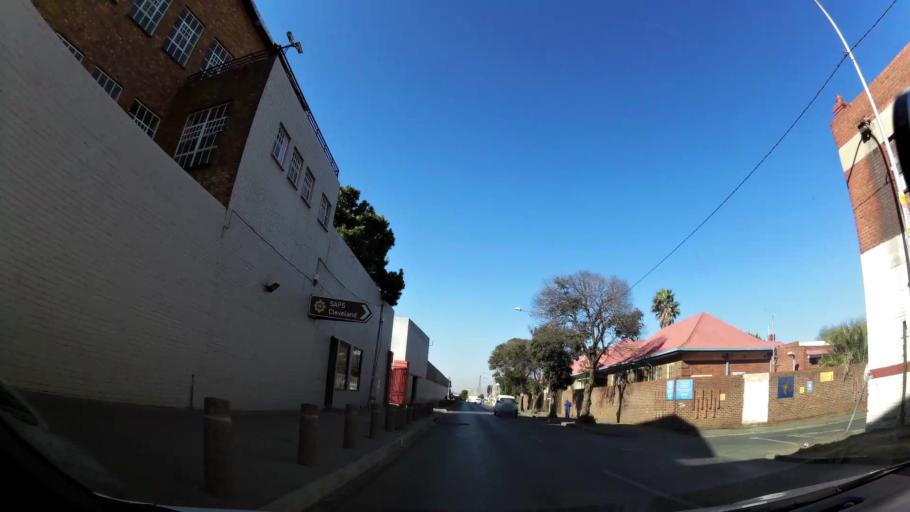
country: ZA
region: Gauteng
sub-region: Ekurhuleni Metropolitan Municipality
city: Germiston
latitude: -26.2031
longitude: 28.1157
